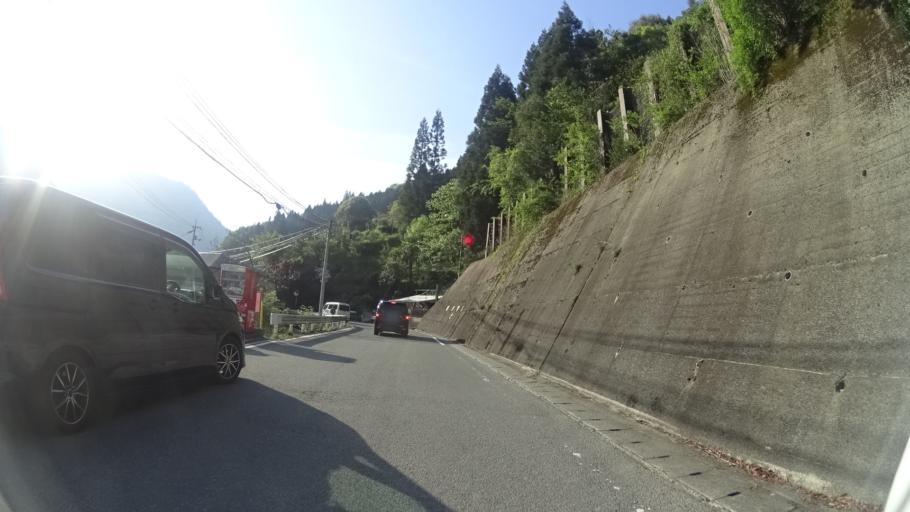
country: JP
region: Tokushima
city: Ikedacho
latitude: 33.8760
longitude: 133.8312
